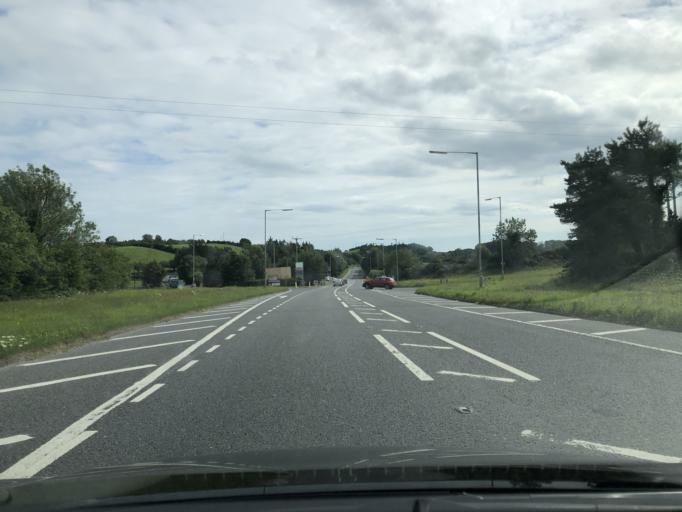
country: GB
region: Northern Ireland
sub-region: Down District
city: Dundrum
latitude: 54.3354
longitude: -5.8362
